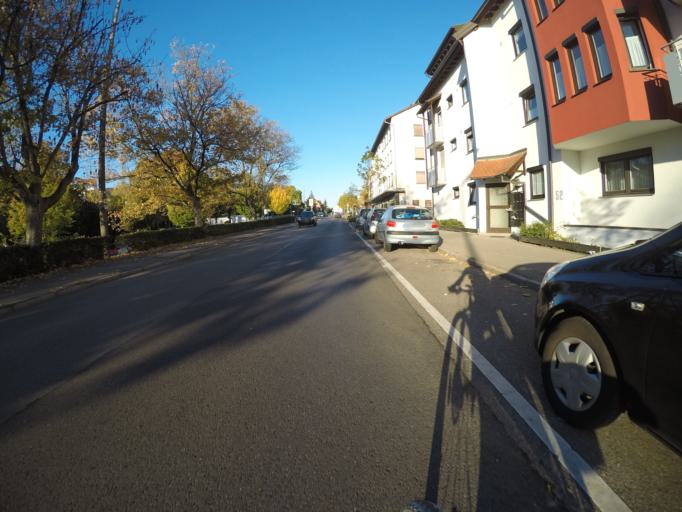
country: DE
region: Baden-Wuerttemberg
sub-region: Regierungsbezirk Stuttgart
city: Boeblingen
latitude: 48.6893
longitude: 9.0180
